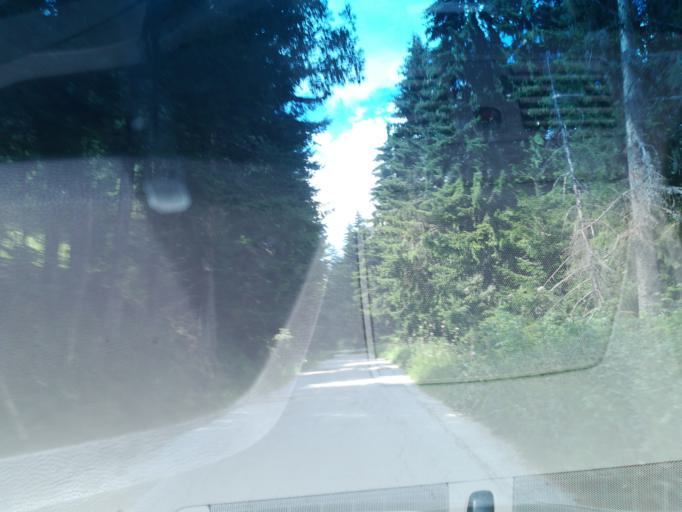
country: BG
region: Smolyan
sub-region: Obshtina Chepelare
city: Chepelare
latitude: 41.6766
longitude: 24.7731
